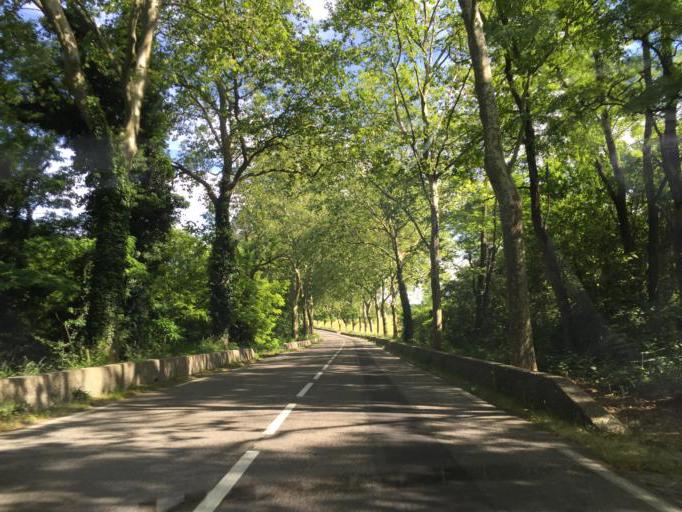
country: FR
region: Rhone-Alpes
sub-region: Departement de la Drome
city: Saulce-sur-Rhone
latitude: 44.6969
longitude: 4.7694
